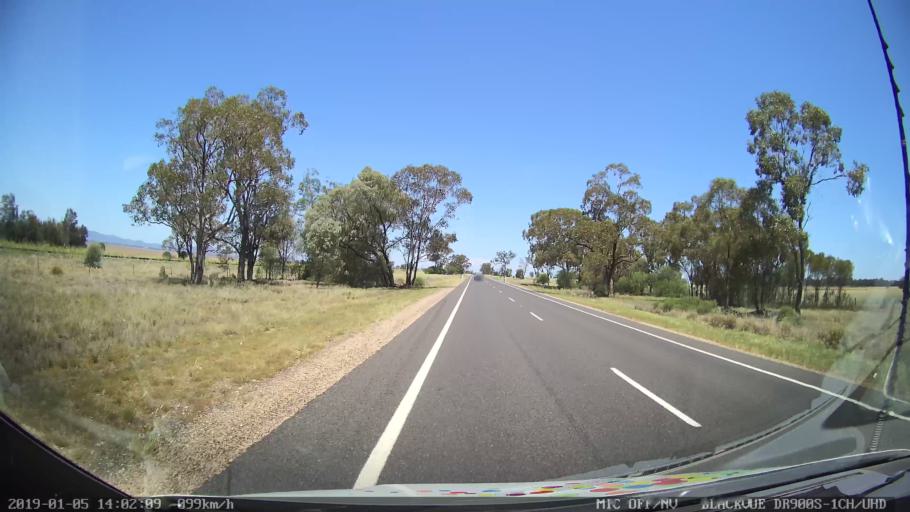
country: AU
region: New South Wales
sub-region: Gunnedah
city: Gunnedah
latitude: -31.1769
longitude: 150.3342
